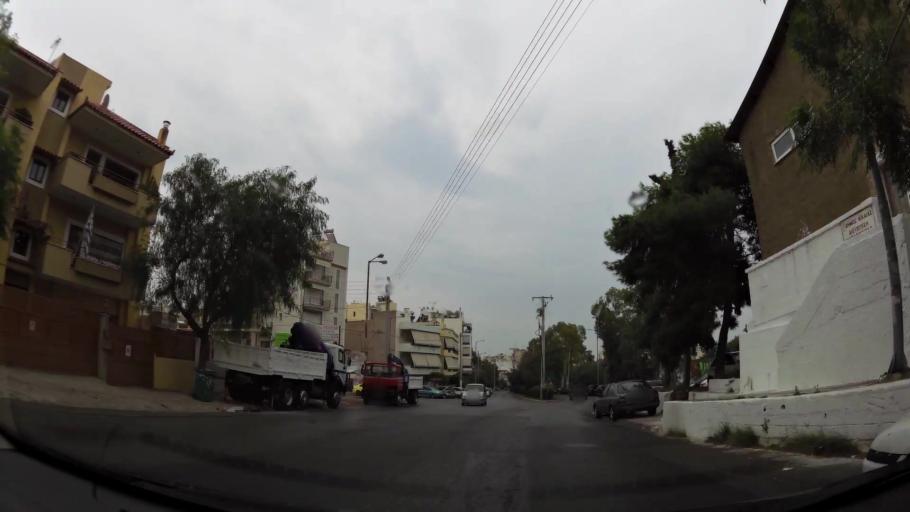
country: GR
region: Attica
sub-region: Nomos Piraios
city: Korydallos
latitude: 37.9843
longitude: 23.6419
